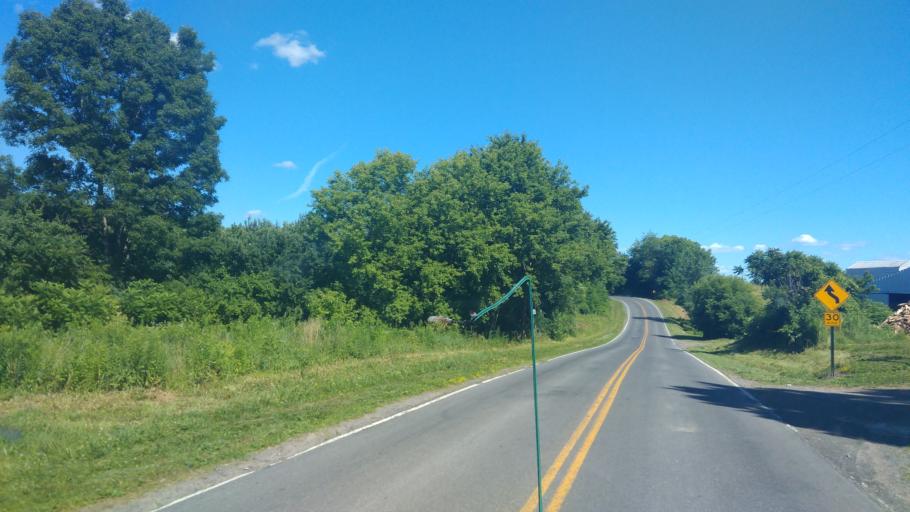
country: US
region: New York
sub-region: Wayne County
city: Clyde
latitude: 43.0243
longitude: -76.8258
